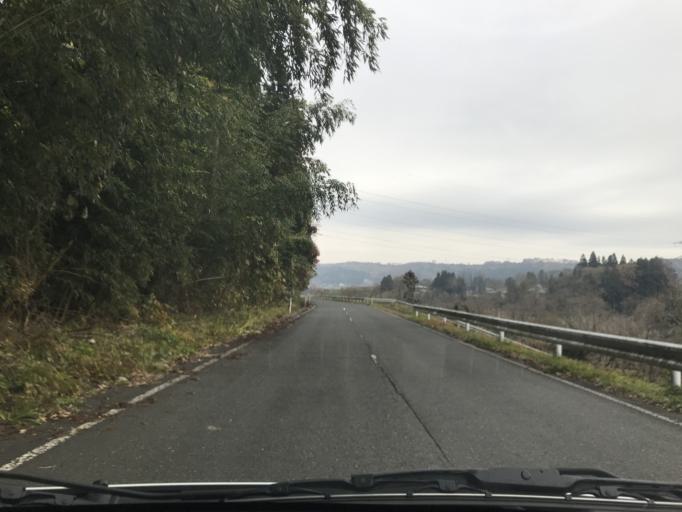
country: JP
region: Iwate
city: Ichinoseki
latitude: 39.0197
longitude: 141.0742
